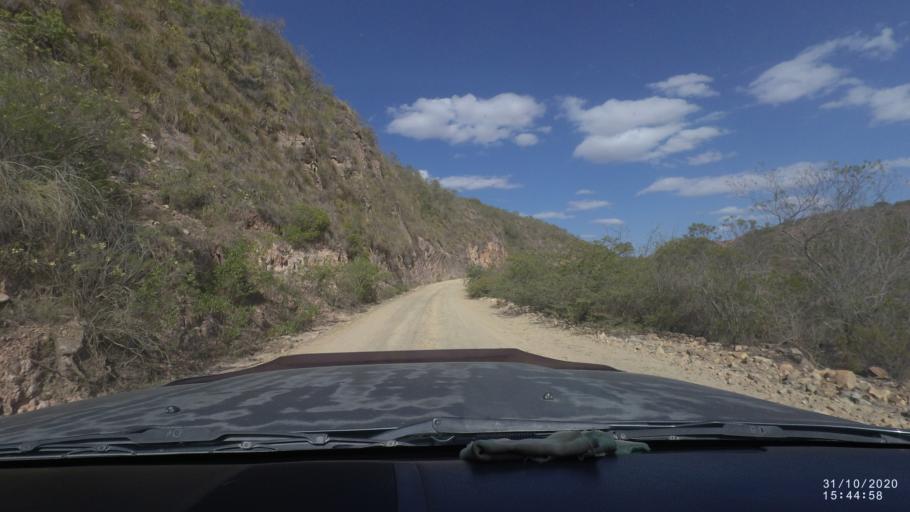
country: BO
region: Chuquisaca
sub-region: Provincia Zudanez
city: Mojocoya
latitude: -18.3180
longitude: -64.7199
